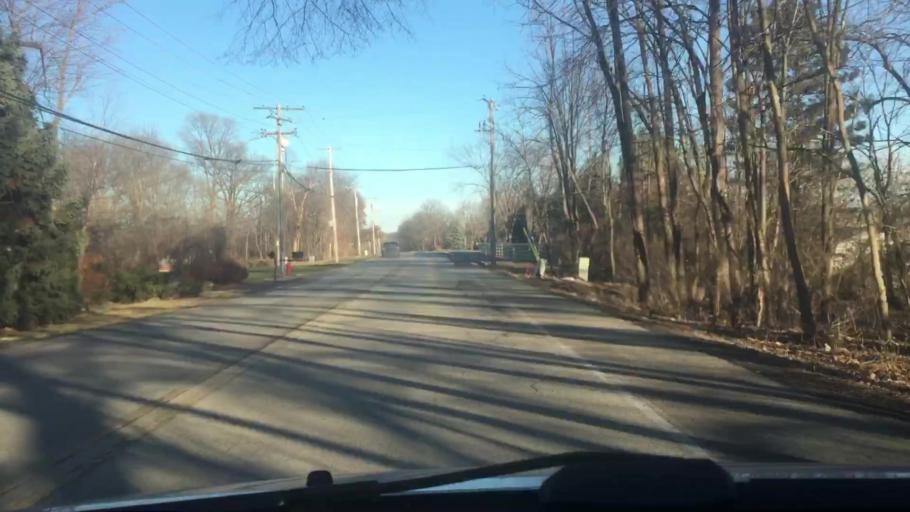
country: US
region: Wisconsin
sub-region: Waukesha County
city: Brookfield
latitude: 43.0593
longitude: -88.1767
